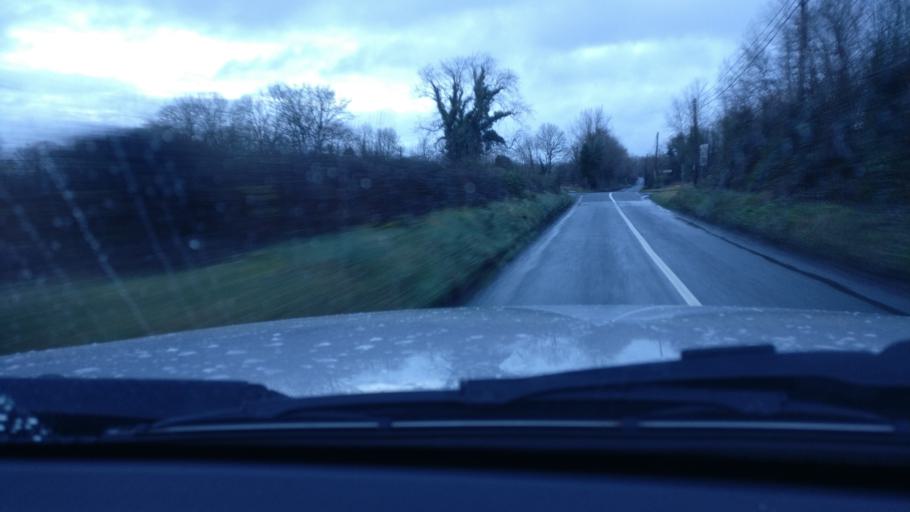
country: IE
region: Connaught
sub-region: County Galway
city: Ballinasloe
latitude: 53.2655
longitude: -8.2534
